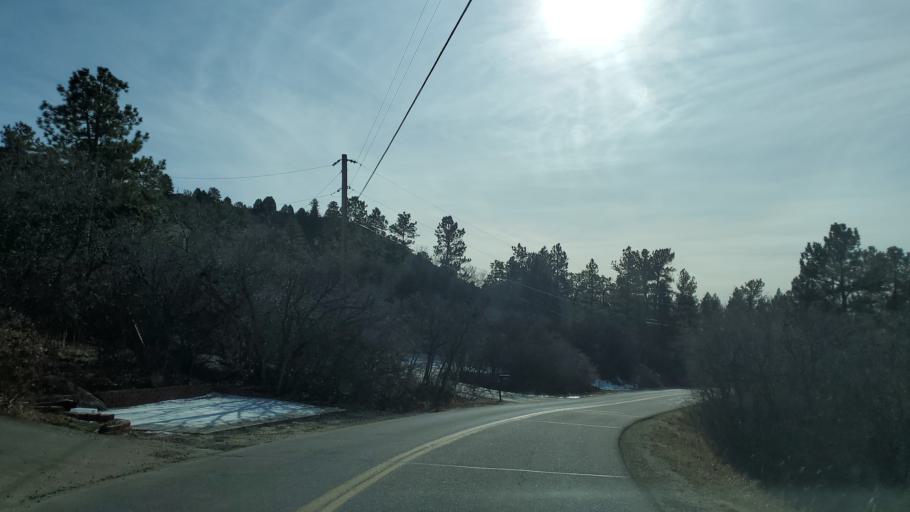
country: US
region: Colorado
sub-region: Douglas County
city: Castle Pines
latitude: 39.4399
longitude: -104.8732
